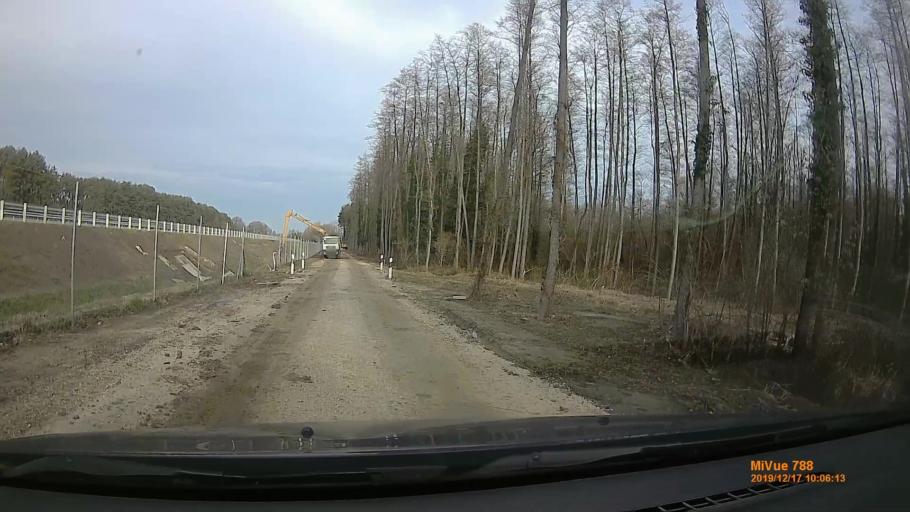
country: HU
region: Somogy
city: Karad
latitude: 46.6444
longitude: 17.7873
